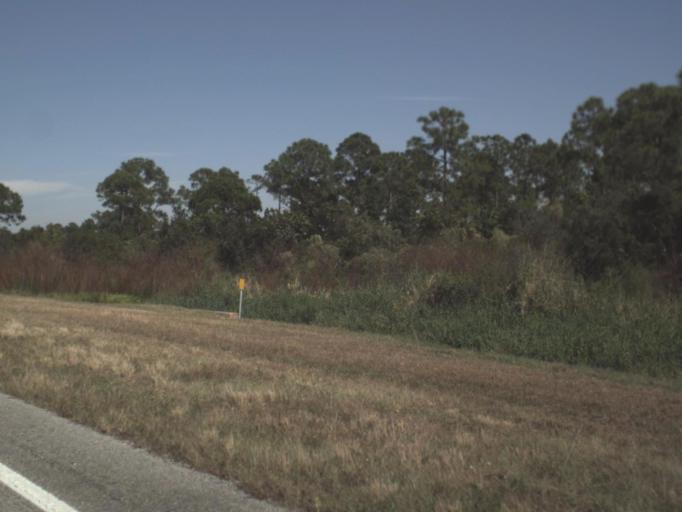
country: US
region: Florida
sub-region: Highlands County
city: Placid Lakes
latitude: 27.0696
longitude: -81.3364
